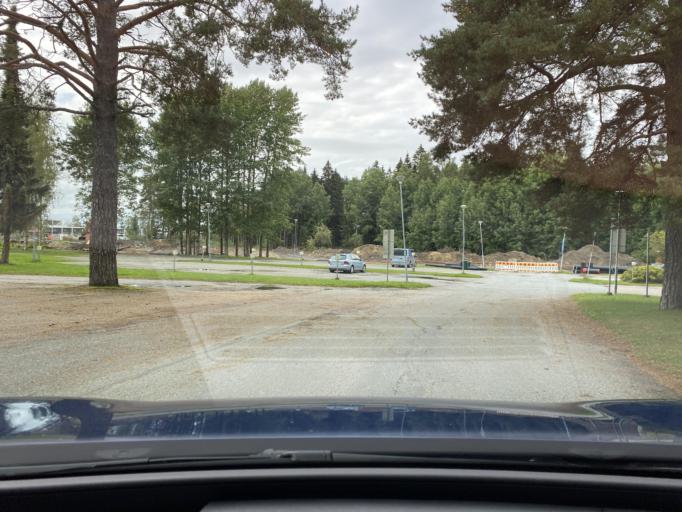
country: FI
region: Pirkanmaa
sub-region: Lounais-Pirkanmaa
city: Vammala
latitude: 61.3344
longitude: 22.9302
